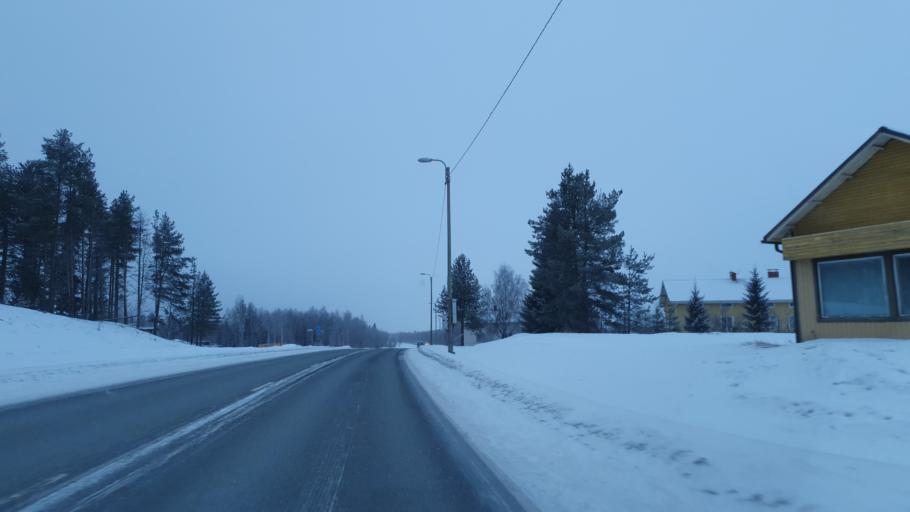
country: SE
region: Norrbotten
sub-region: Overtornea Kommun
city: OEvertornea
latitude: 66.3654
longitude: 23.6959
